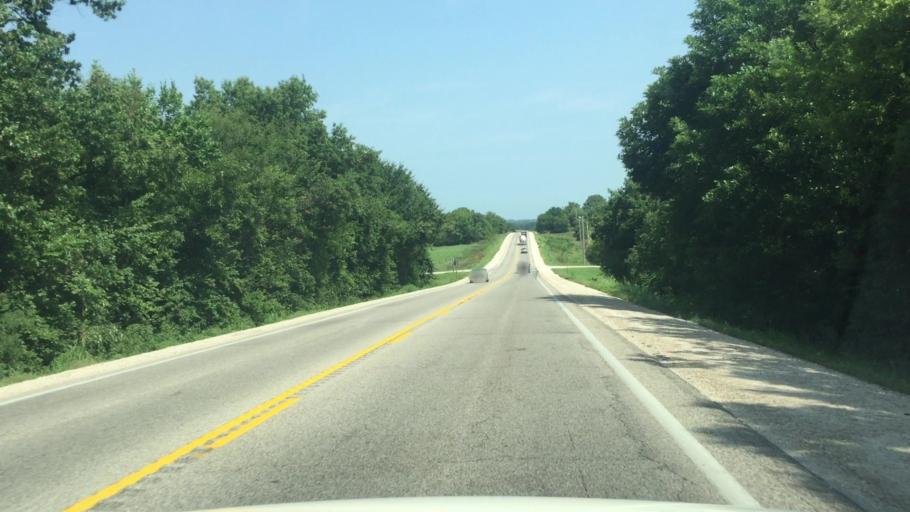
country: US
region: Kansas
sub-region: Montgomery County
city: Cherryvale
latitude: 37.1529
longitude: -95.5768
